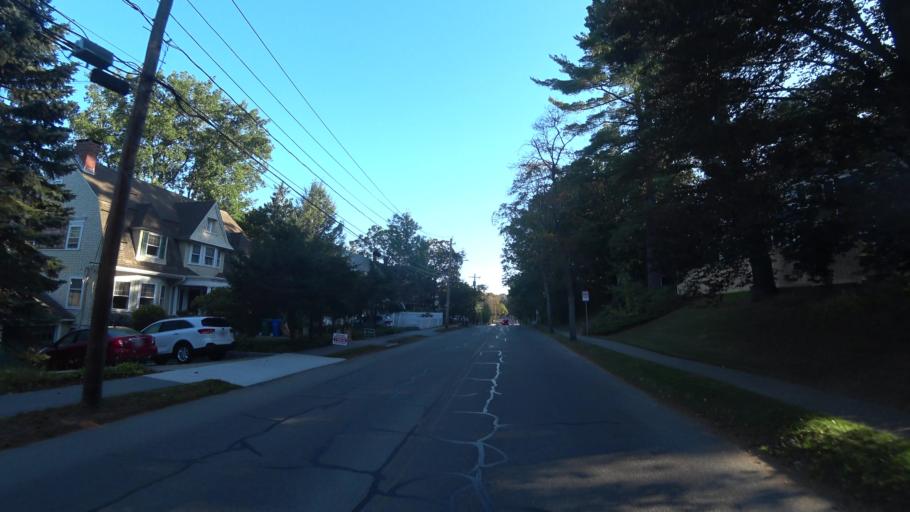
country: US
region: Massachusetts
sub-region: Middlesex County
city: Newton
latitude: 42.3353
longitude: -71.1870
